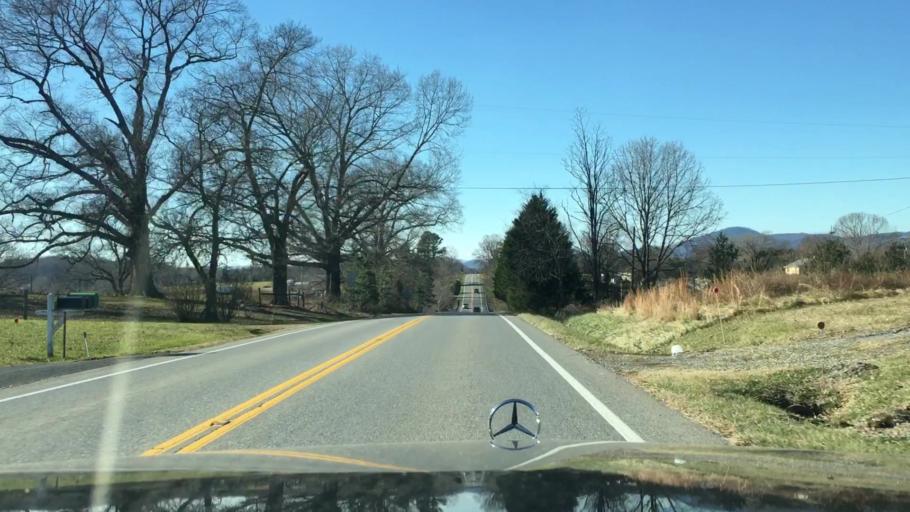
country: US
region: Virginia
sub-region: Botetourt County
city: Blue Ridge
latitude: 37.2528
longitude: -79.7058
